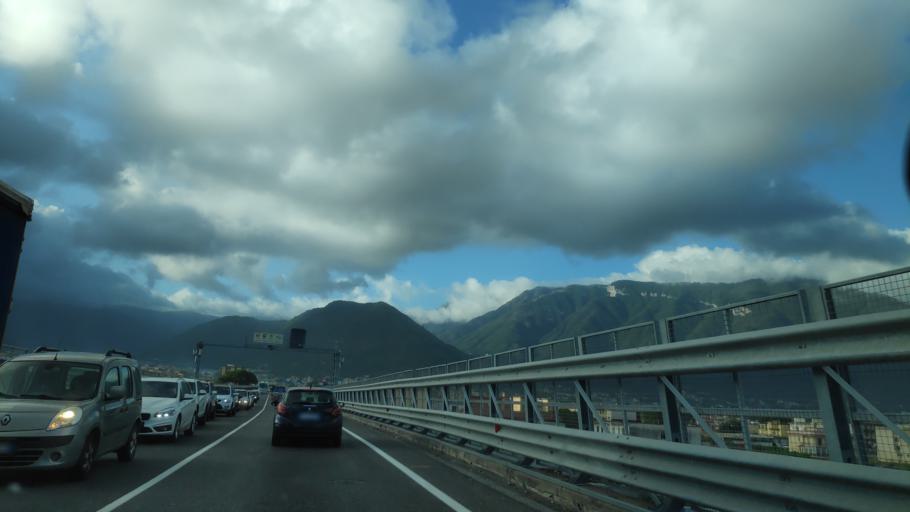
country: IT
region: Campania
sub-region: Provincia di Napoli
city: Castellammare di Stabia
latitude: 40.7161
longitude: 14.4948
